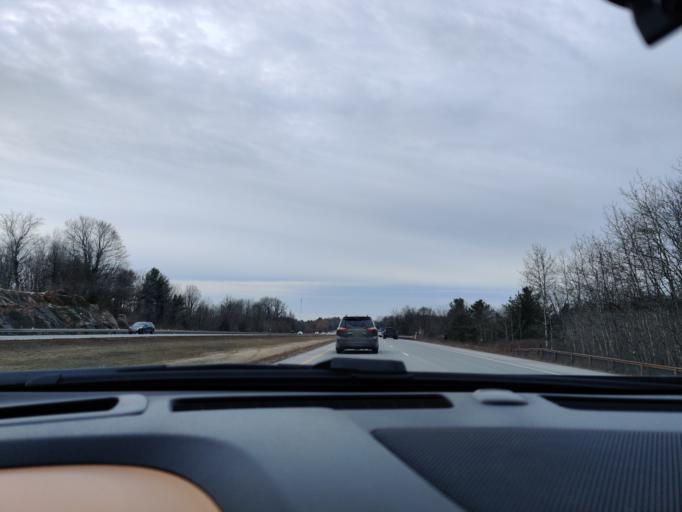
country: US
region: New York
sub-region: Jefferson County
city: Alexandria Bay
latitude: 44.3926
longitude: -75.9572
